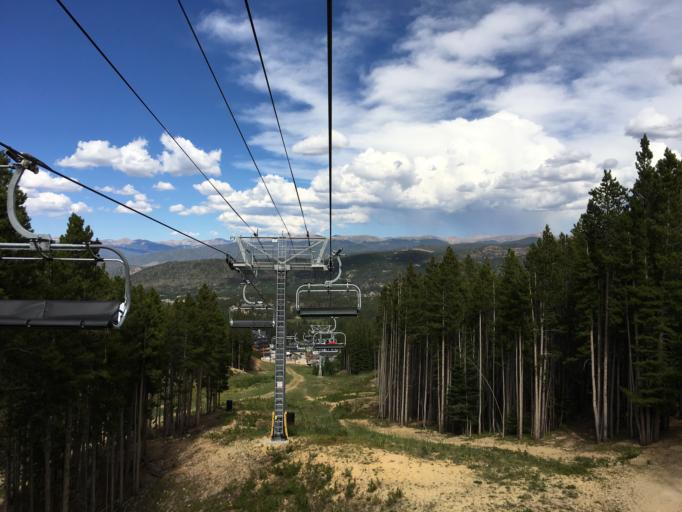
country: US
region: Colorado
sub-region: Summit County
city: Breckenridge
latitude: 39.4774
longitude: -106.0738
